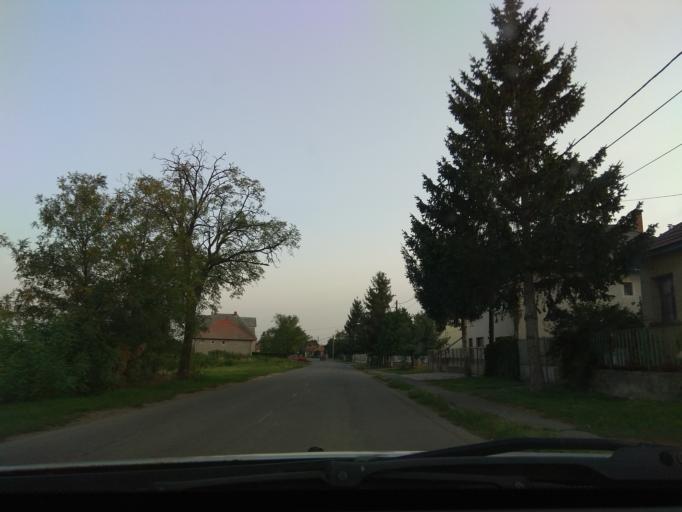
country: HU
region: Borsod-Abauj-Zemplen
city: Szerencs
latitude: 48.1951
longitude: 21.2148
